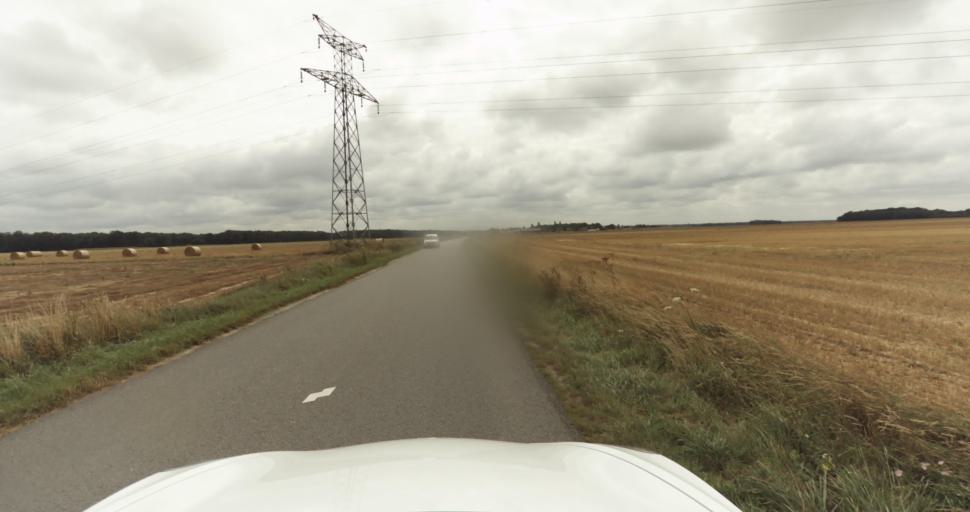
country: FR
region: Haute-Normandie
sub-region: Departement de l'Eure
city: Claville
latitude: 49.0361
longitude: 1.0273
